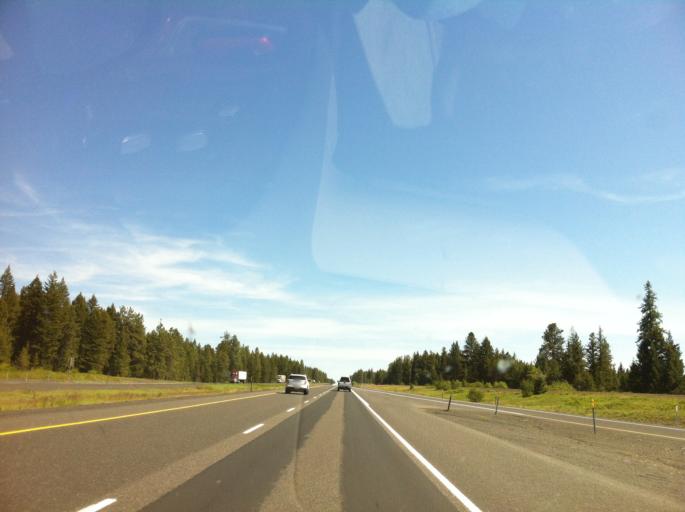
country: US
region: Oregon
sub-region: Umatilla County
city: Mission
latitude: 45.5063
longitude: -118.4261
